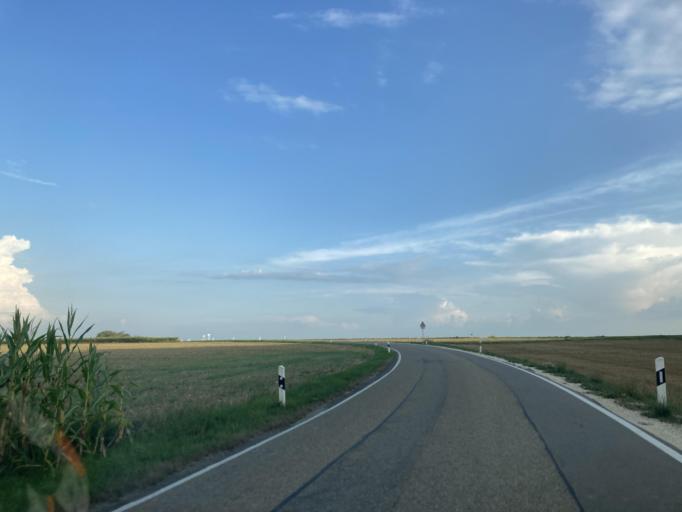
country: DE
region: Bavaria
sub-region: Swabia
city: Medlingen
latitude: 48.5830
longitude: 10.3075
